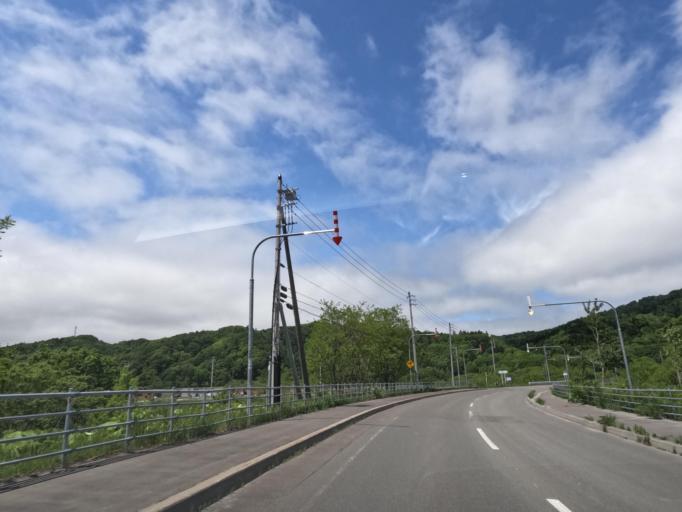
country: JP
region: Hokkaido
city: Tobetsu
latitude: 43.3140
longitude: 141.5568
